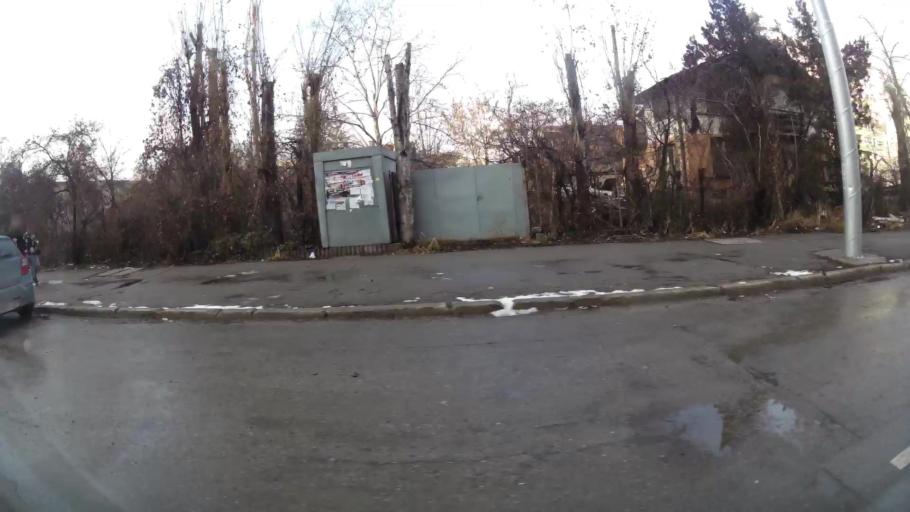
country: BG
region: Sofia-Capital
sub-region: Stolichna Obshtina
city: Sofia
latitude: 42.7180
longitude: 23.2699
